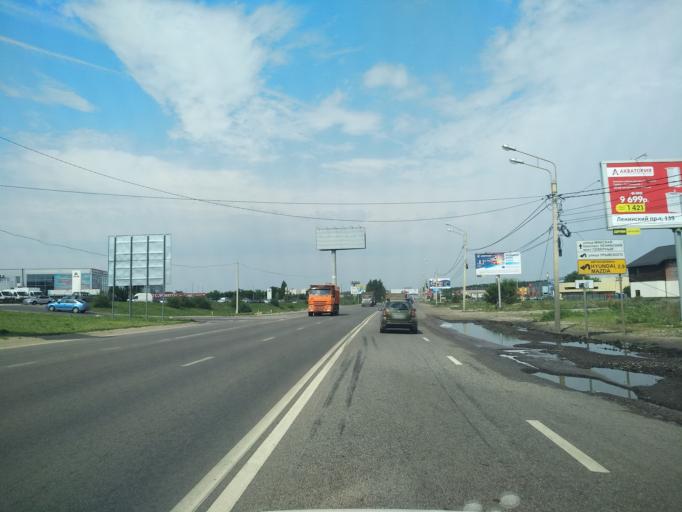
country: RU
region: Voronezj
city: Somovo
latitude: 51.6787
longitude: 39.2924
